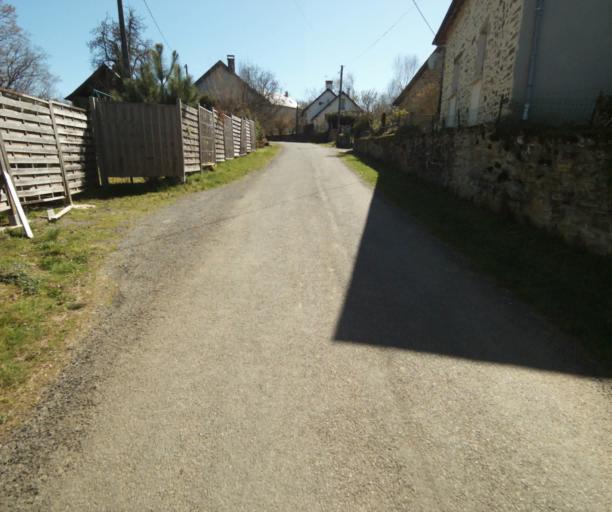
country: FR
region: Limousin
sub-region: Departement de la Correze
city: Uzerche
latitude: 45.4075
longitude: 1.6168
